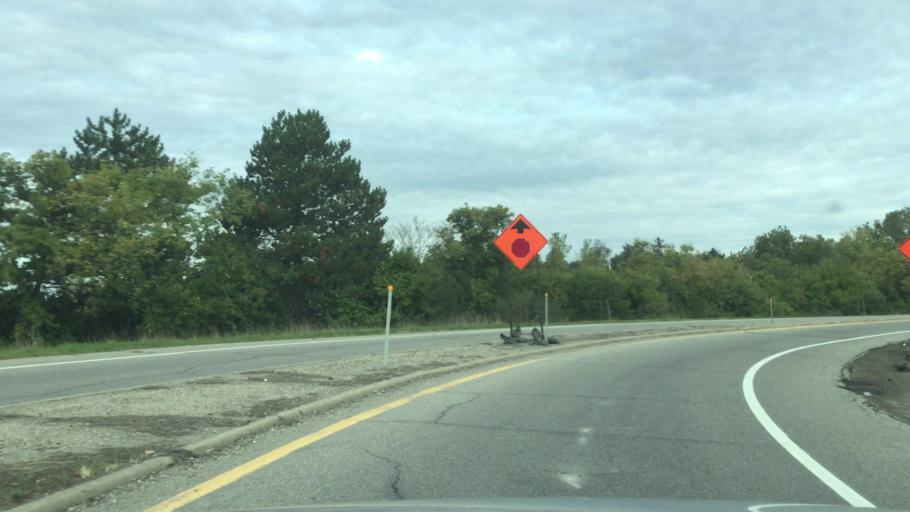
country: US
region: Michigan
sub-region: Genesee County
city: Flint
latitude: 42.9718
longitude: -83.7275
